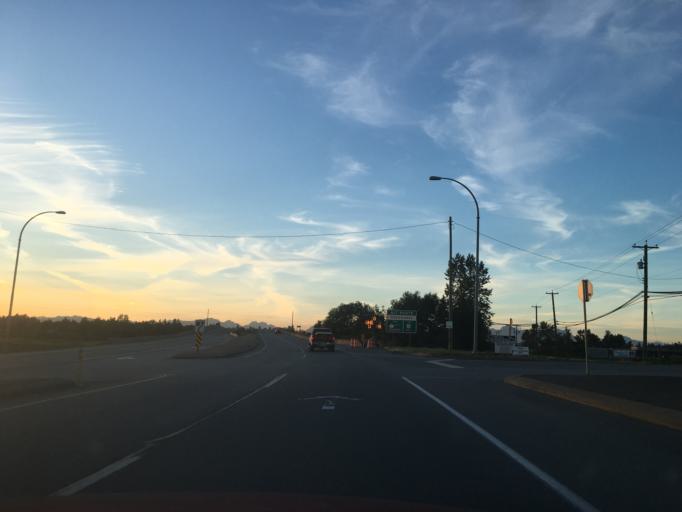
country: CA
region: British Columbia
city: Langley
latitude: 49.0971
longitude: -122.7351
